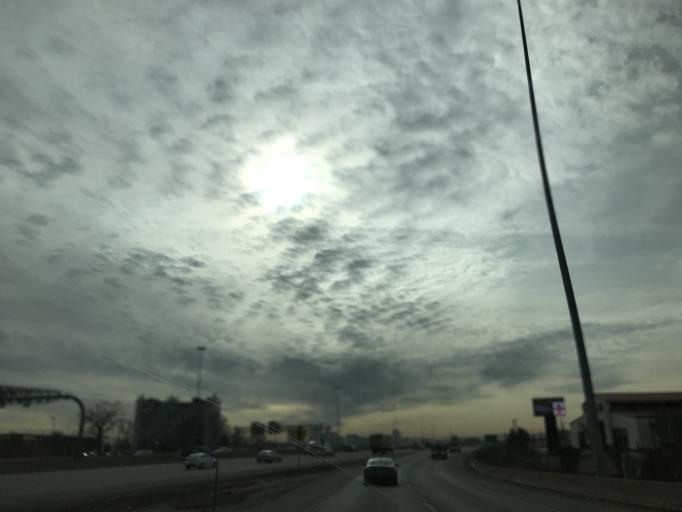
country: US
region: Colorado
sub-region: Adams County
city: Twin Lakes
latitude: 39.8007
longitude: -104.9859
